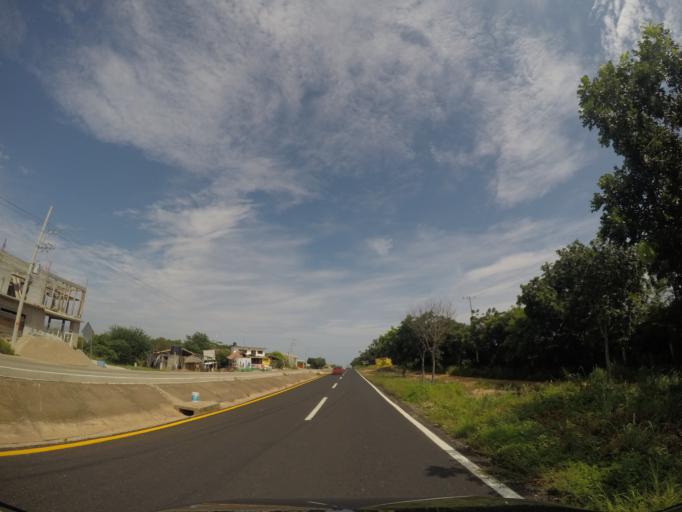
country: MX
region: Oaxaca
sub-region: Santa Maria Colotepec
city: Brisas de Zicatela
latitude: 15.8226
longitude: -97.0167
